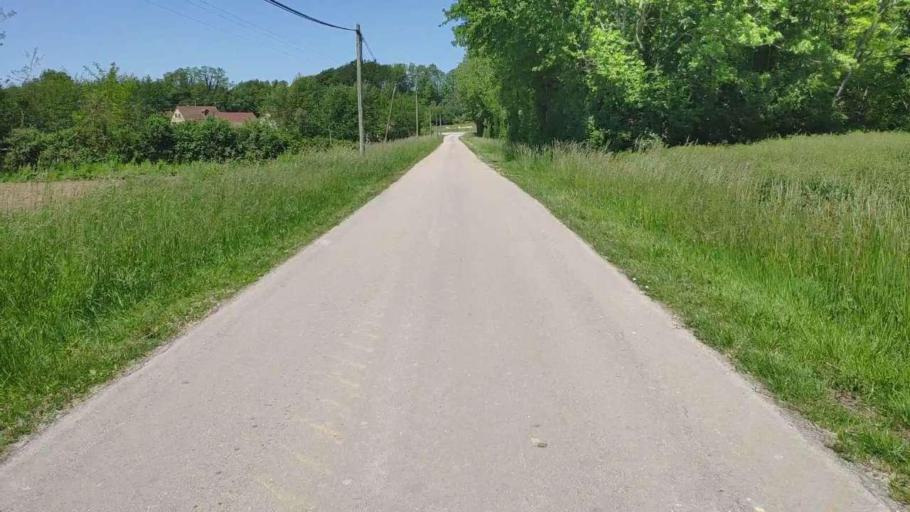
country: FR
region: Franche-Comte
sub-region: Departement du Jura
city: Bletterans
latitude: 46.7600
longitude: 5.4214
